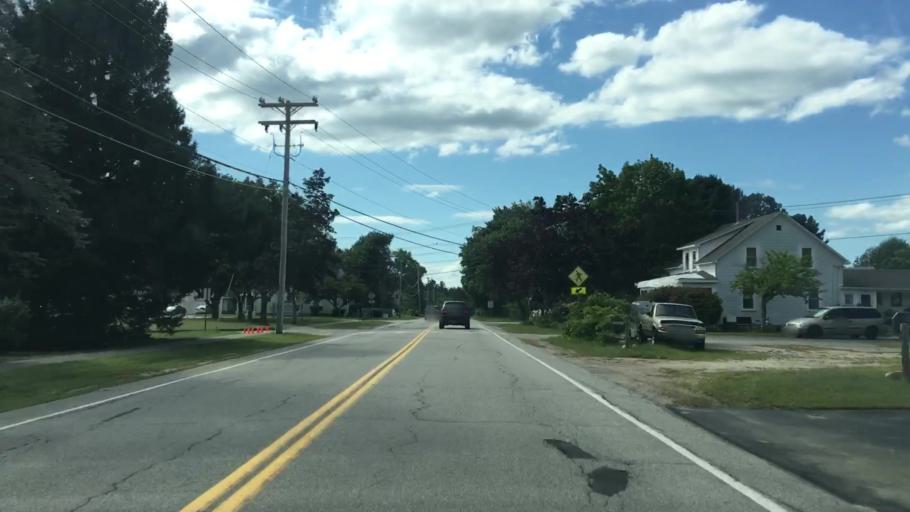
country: US
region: New Hampshire
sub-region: Strafford County
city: Somersworth
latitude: 43.2592
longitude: -70.8785
